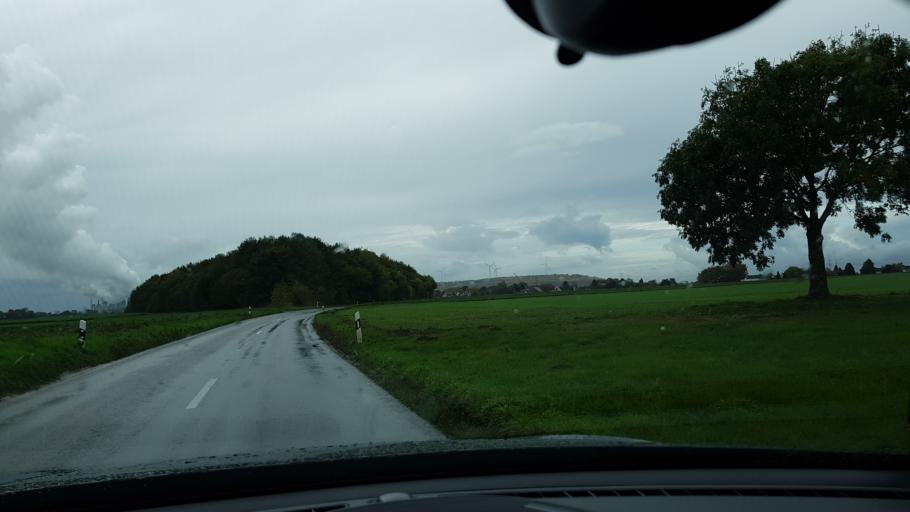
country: DE
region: North Rhine-Westphalia
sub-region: Regierungsbezirk Dusseldorf
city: Rommerskirchen
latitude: 51.0707
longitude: 6.6868
